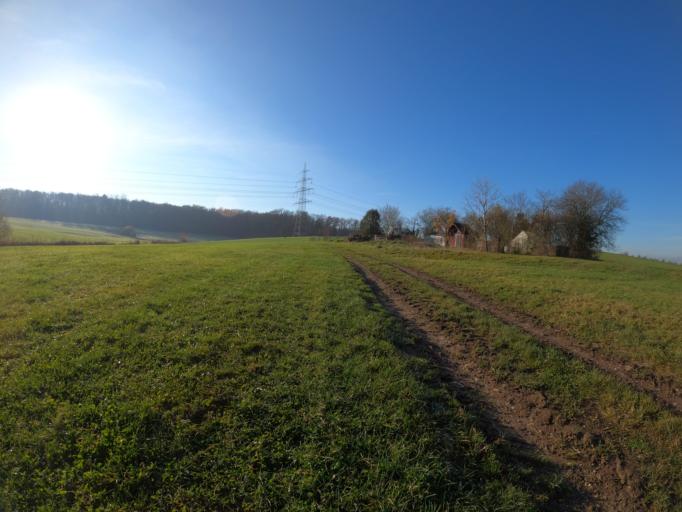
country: DE
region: Baden-Wuerttemberg
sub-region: Regierungsbezirk Stuttgart
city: Albershausen
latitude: 48.7050
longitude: 9.5531
